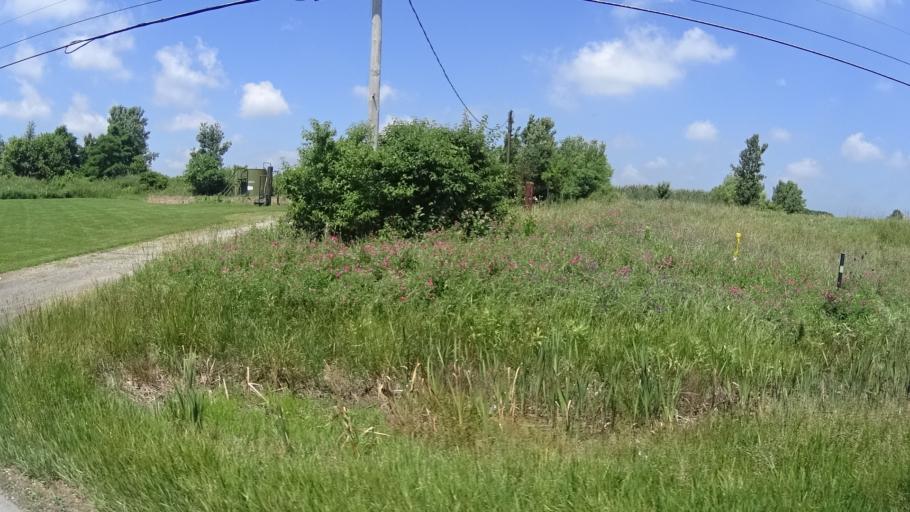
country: US
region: Ohio
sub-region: Huron County
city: Wakeman
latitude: 41.3296
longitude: -82.3664
